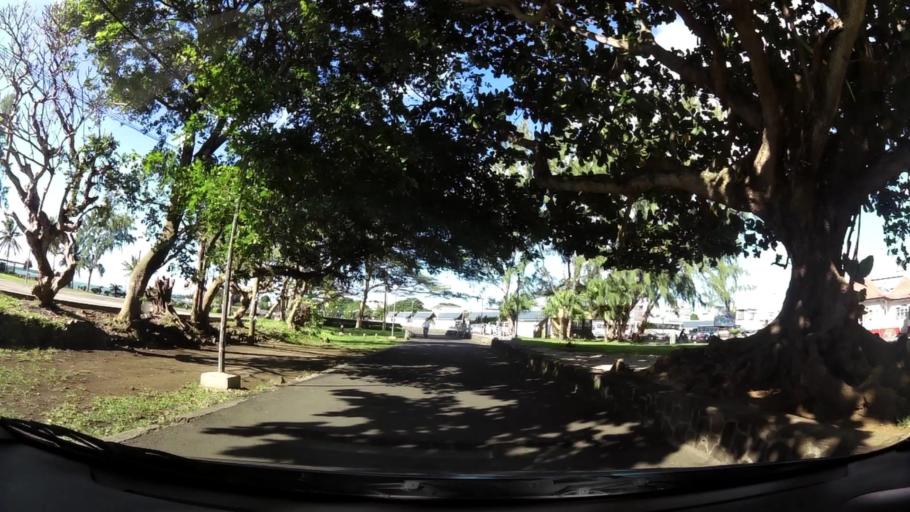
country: MU
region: Grand Port
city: Mahebourg
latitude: -20.4056
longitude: 57.7091
